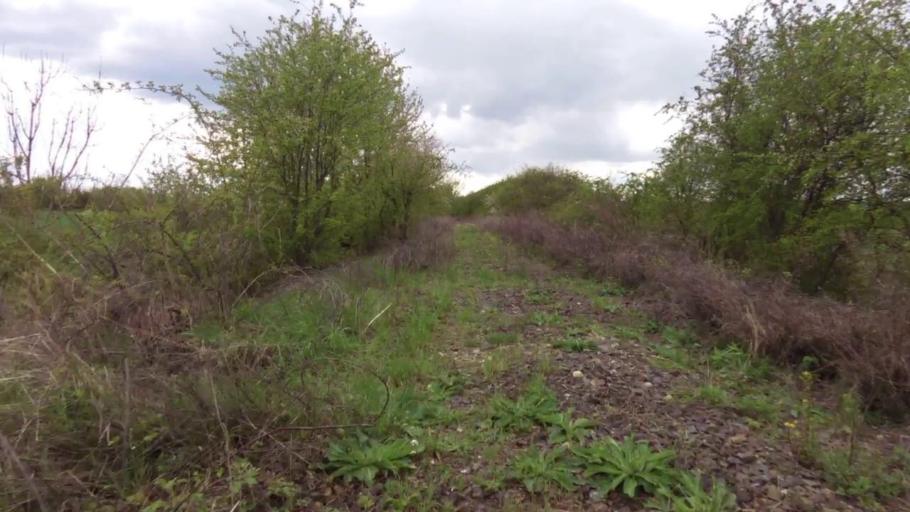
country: PL
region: West Pomeranian Voivodeship
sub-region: Powiat choszczenski
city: Pelczyce
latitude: 53.0465
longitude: 15.2950
